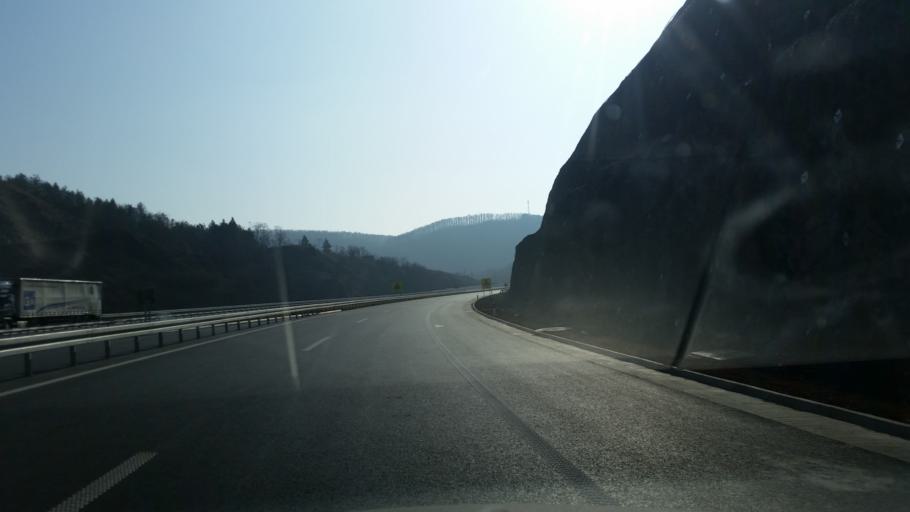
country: RS
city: Prislonica
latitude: 43.9867
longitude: 20.4019
